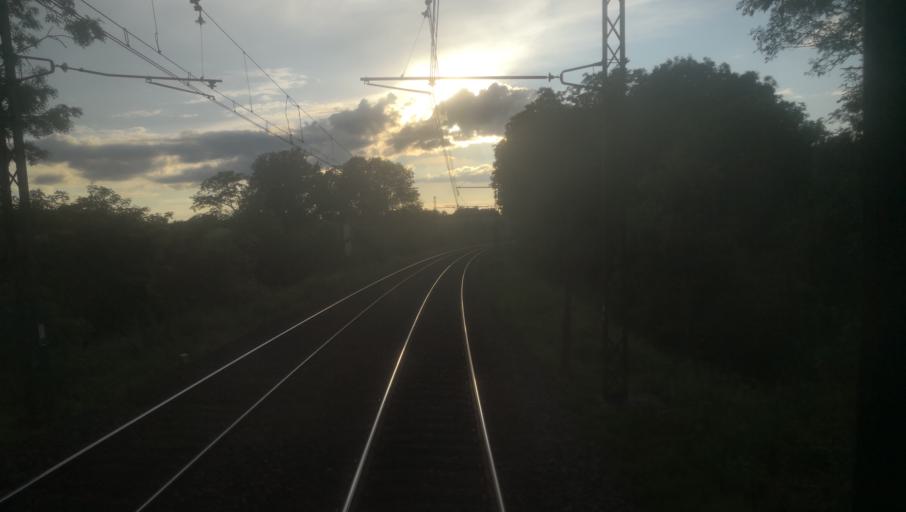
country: FR
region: Centre
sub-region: Departement de l'Indre
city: Le Pechereau
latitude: 46.5016
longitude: 1.5073
